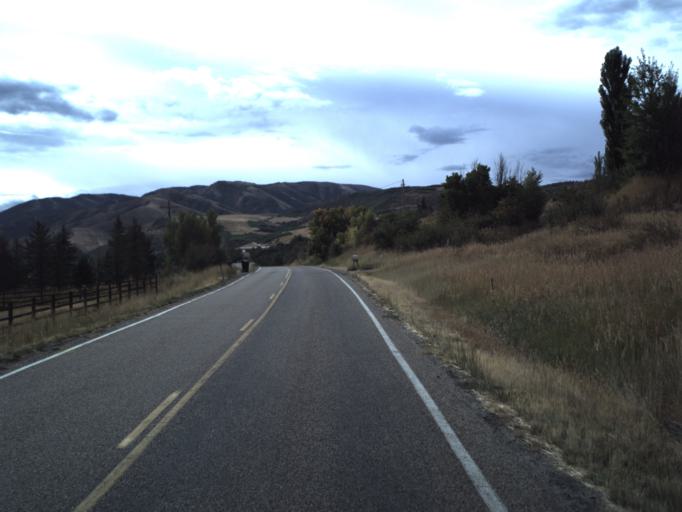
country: US
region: Utah
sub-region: Morgan County
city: Morgan
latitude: 40.9581
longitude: -111.6671
